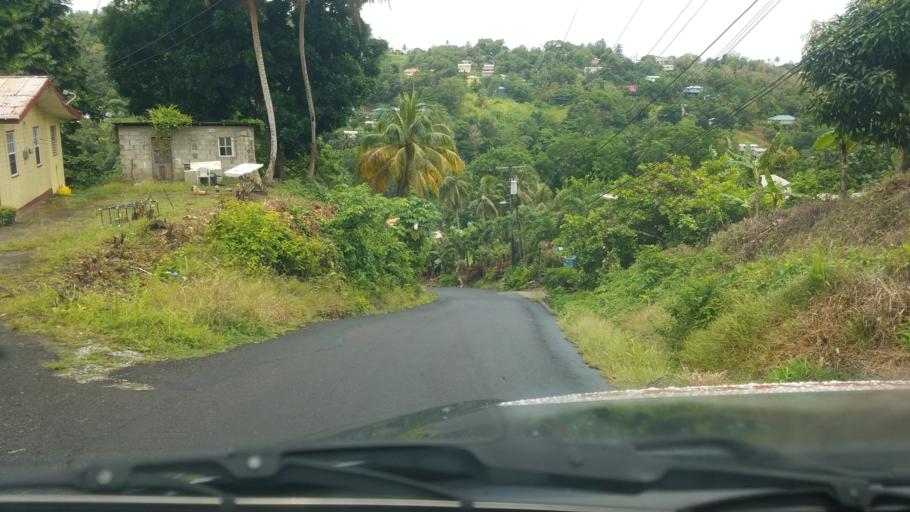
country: LC
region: Castries Quarter
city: Bisee
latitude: 14.0002
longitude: -60.9604
